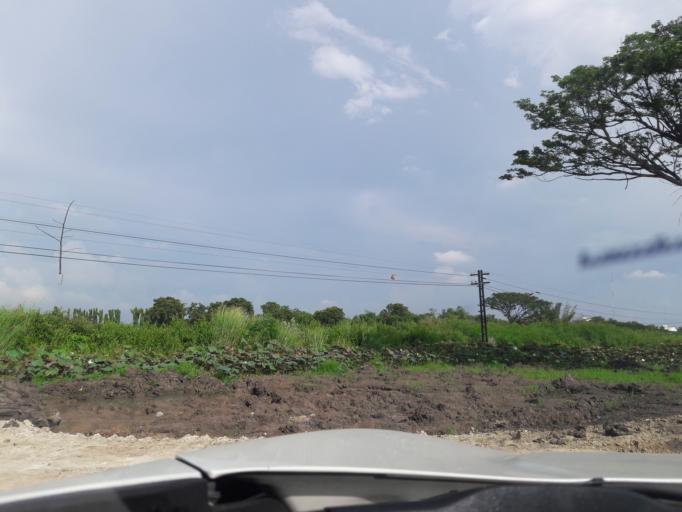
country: TH
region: Lop Buri
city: Ban Mi
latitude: 15.0483
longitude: 100.5318
